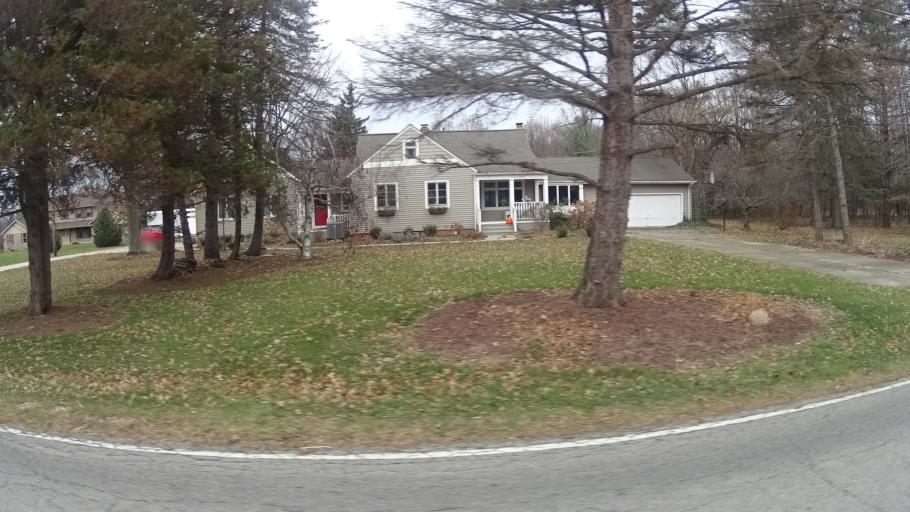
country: US
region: Ohio
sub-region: Cuyahoga County
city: Strongsville
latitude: 41.2894
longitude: -81.8834
